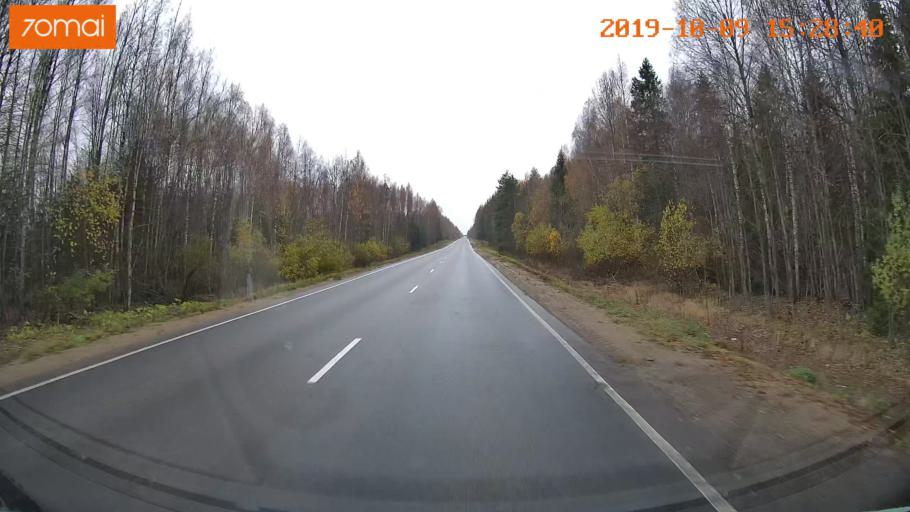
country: RU
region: Kostroma
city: Susanino
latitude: 58.0005
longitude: 41.3561
